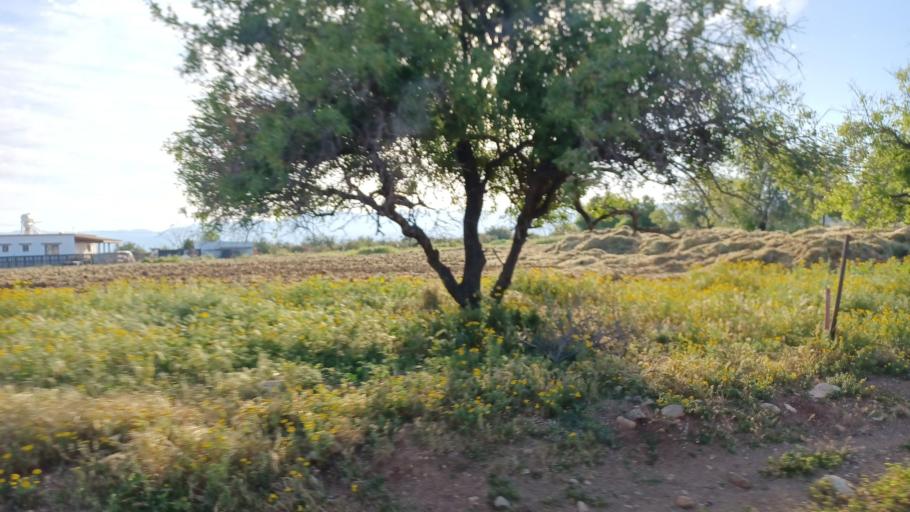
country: CY
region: Pafos
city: Polis
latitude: 35.0319
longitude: 32.3986
